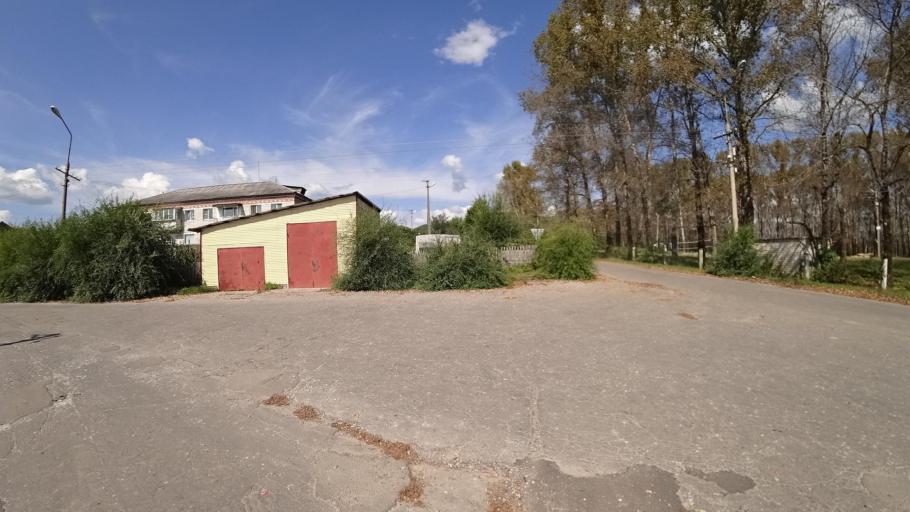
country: RU
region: Jewish Autonomous Oblast
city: Londoko
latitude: 49.0161
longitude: 131.8872
